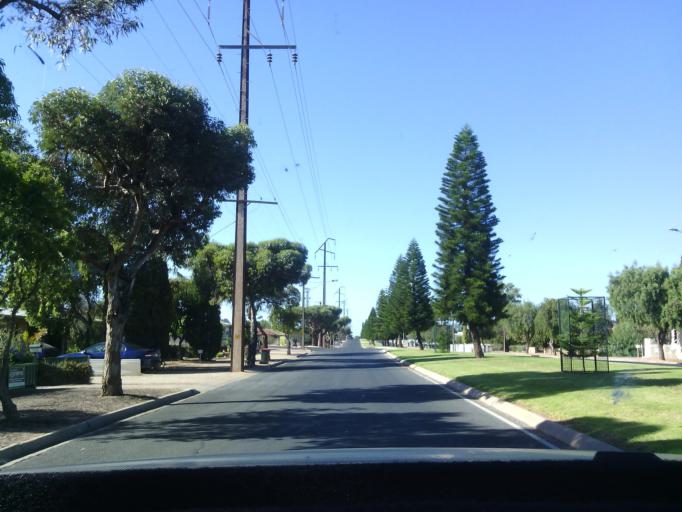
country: AU
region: South Australia
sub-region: Berri and Barmera
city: Berri
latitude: -34.2743
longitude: 140.5971
